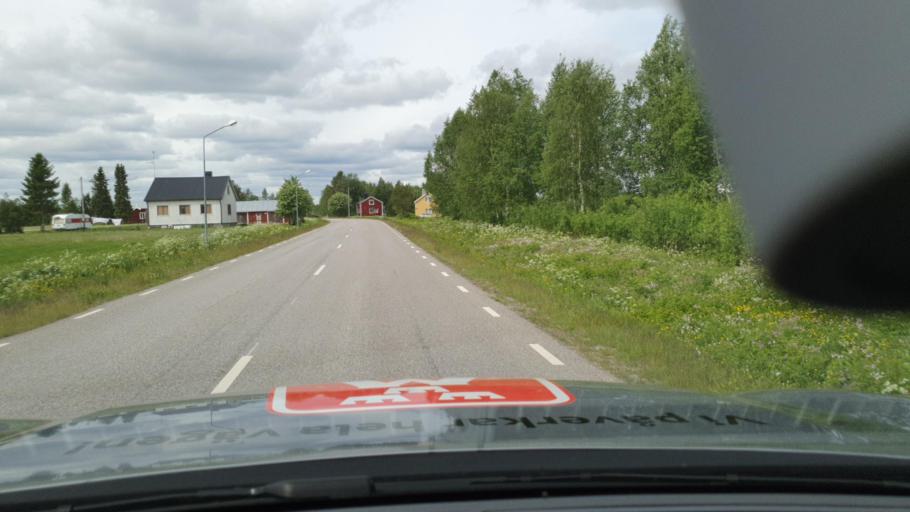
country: FI
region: Lapland
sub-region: Torniolaakso
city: Ylitornio
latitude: 66.0459
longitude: 23.6363
